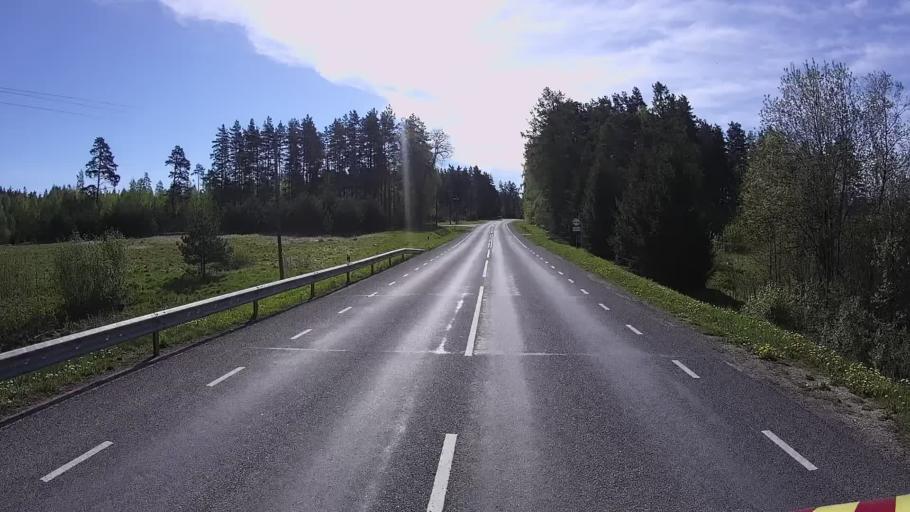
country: EE
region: Polvamaa
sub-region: Polva linn
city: Polva
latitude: 58.1850
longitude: 27.1018
